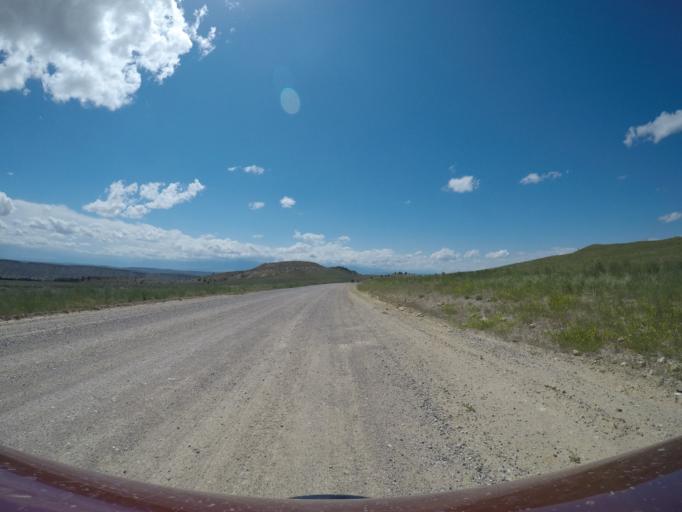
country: US
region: Wyoming
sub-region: Park County
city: Powell
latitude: 45.2064
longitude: -108.7901
